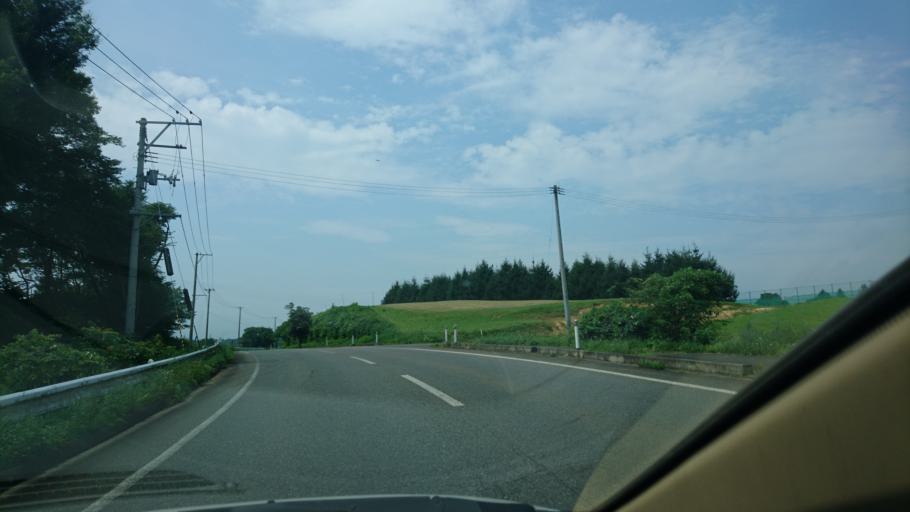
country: JP
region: Iwate
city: Kitakami
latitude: 39.2553
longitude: 141.0896
